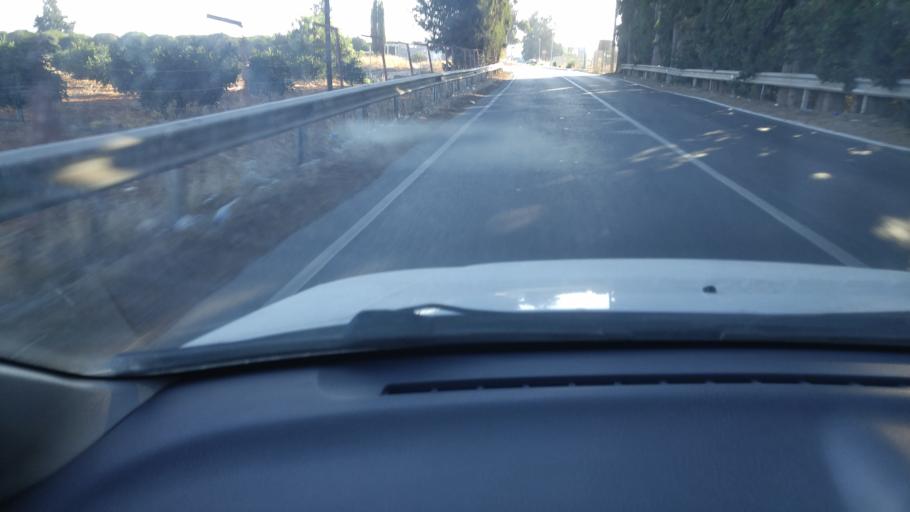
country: CY
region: Limassol
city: Ypsonas
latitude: 34.6555
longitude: 32.9934
